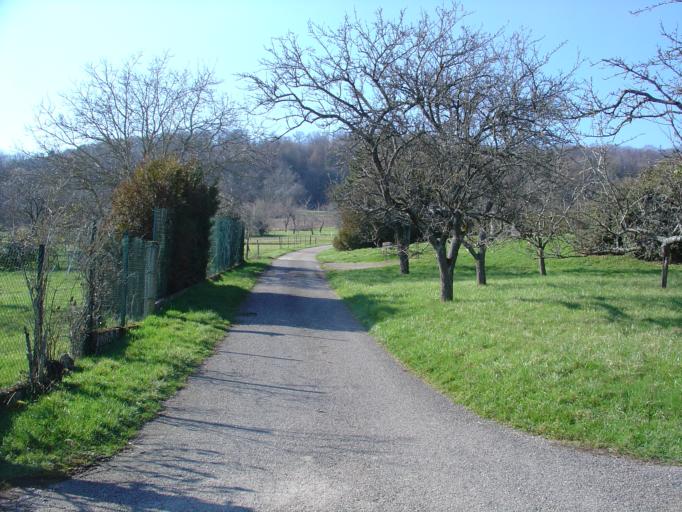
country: FR
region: Lorraine
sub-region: Departement de Meurthe-et-Moselle
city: Blenod-les-Toul
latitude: 48.5438
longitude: 5.8403
